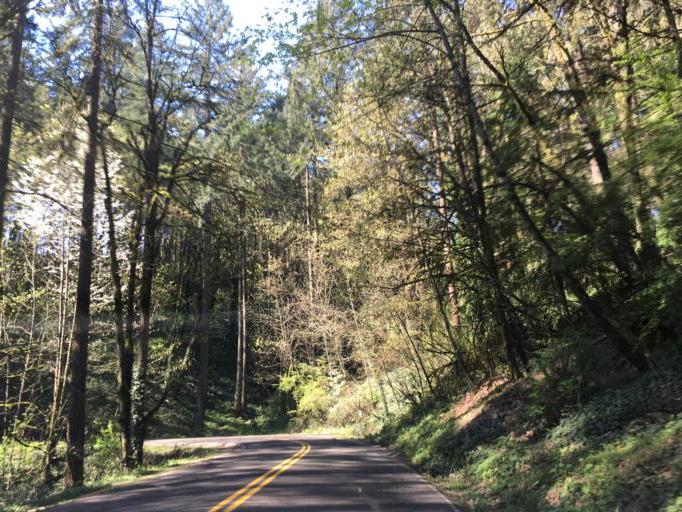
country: US
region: Oregon
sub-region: Multnomah County
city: Portland
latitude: 45.5166
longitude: -122.7077
